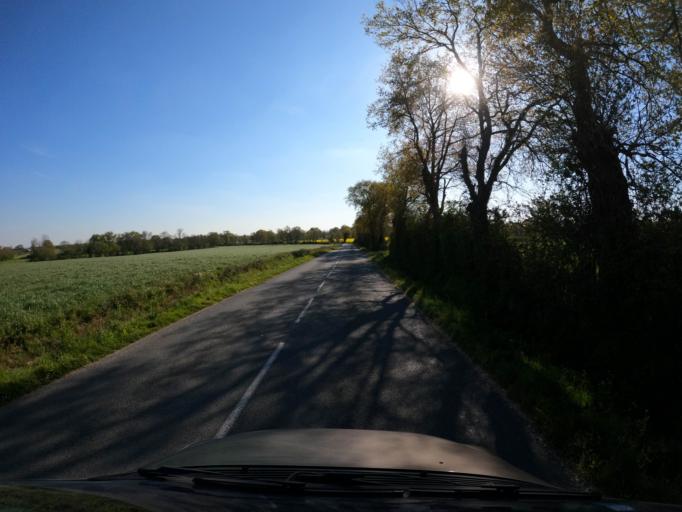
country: FR
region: Pays de la Loire
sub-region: Departement de la Vendee
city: Beaurepaire
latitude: 46.9207
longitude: -1.1198
